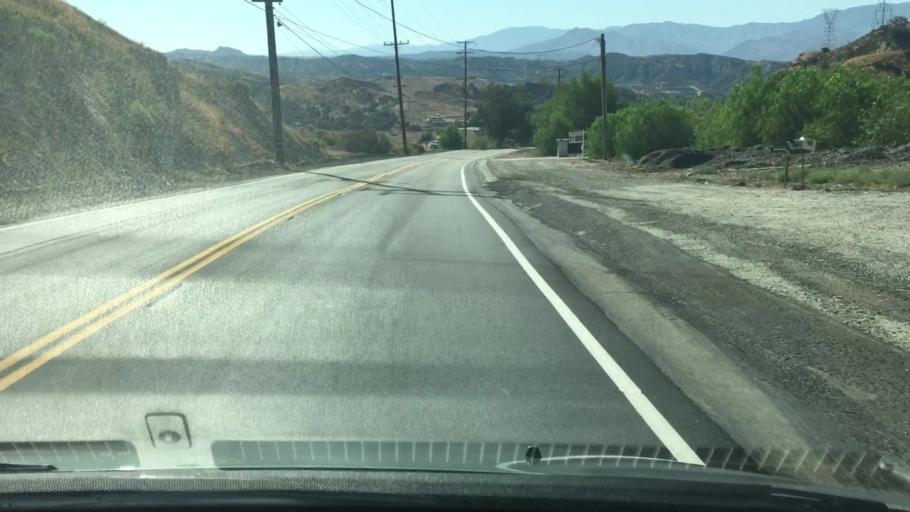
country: US
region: California
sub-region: Los Angeles County
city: Agua Dulce
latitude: 34.4707
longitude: -118.4308
